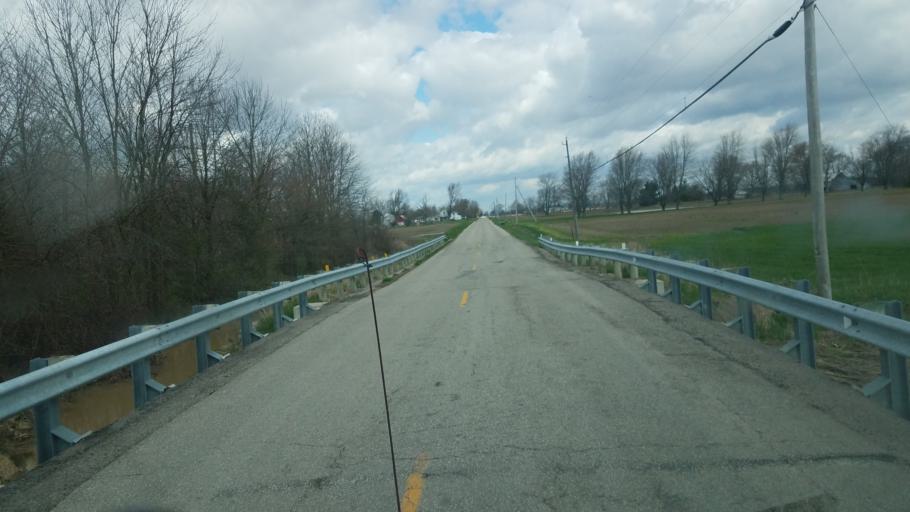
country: US
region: Ohio
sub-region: Union County
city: Richwood
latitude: 40.4007
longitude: -83.3065
